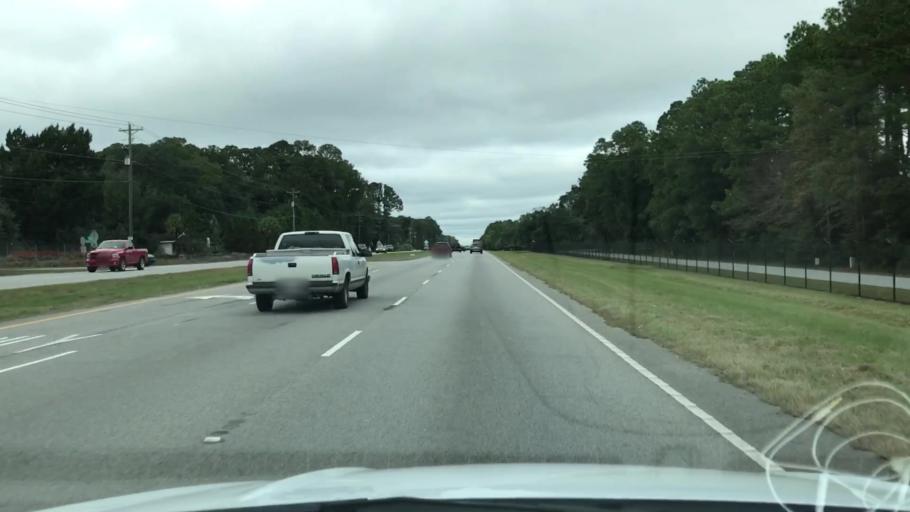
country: US
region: South Carolina
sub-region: Beaufort County
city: Burton
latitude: 32.4845
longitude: -80.7399
